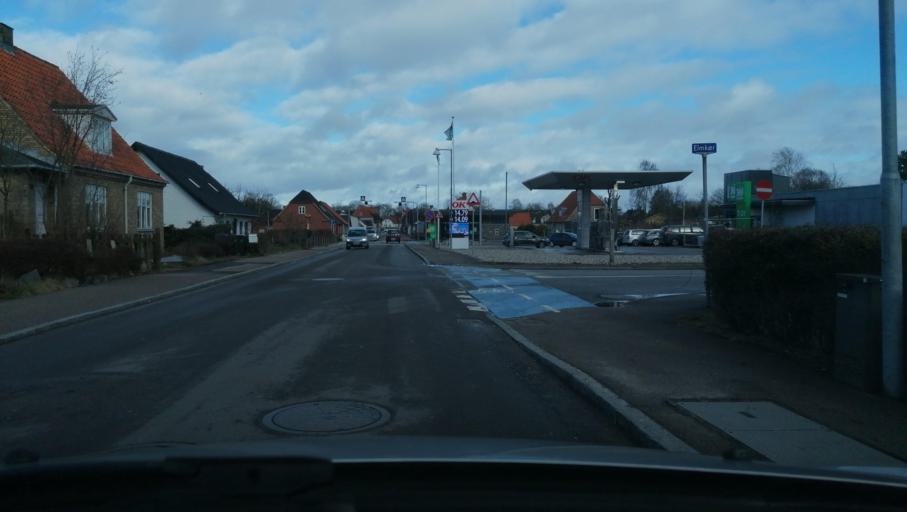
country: DK
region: Zealand
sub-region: Odsherred Kommune
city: Horve
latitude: 55.7523
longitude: 11.4489
